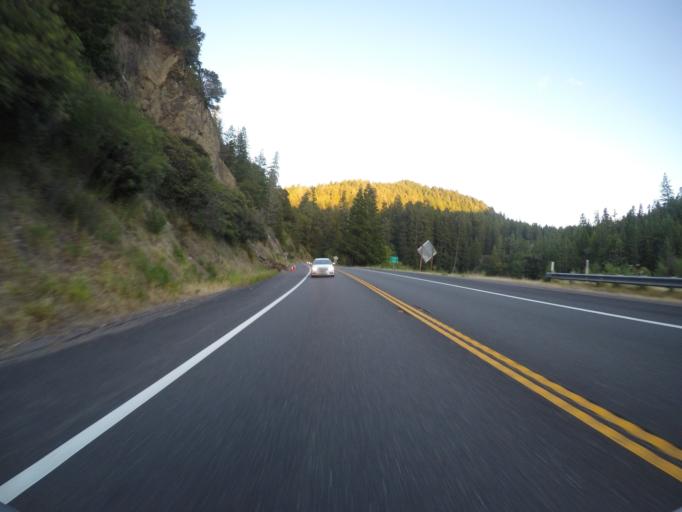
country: US
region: California
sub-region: Humboldt County
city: Redway
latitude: 39.9005
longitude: -123.7541
